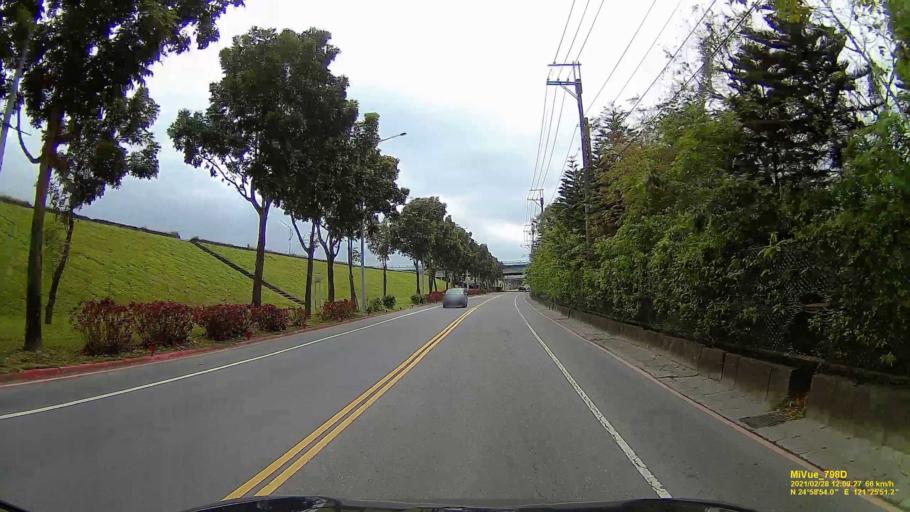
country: TW
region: Taipei
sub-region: Taipei
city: Banqiao
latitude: 24.9815
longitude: 121.4307
